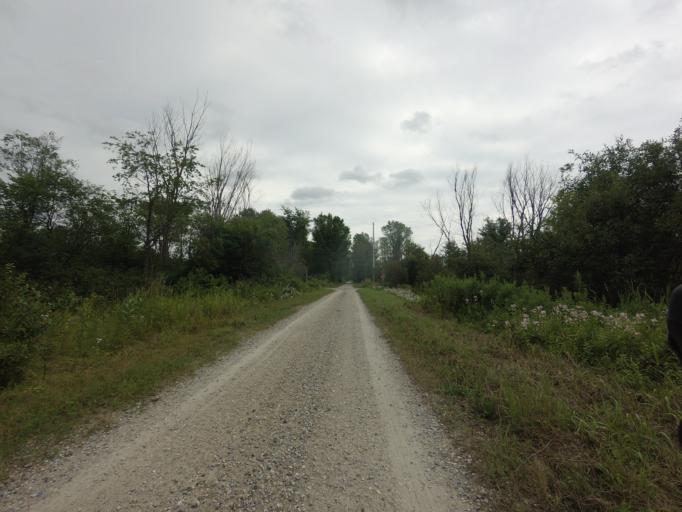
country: CA
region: Ontario
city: Perth
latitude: 44.8209
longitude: -76.5487
